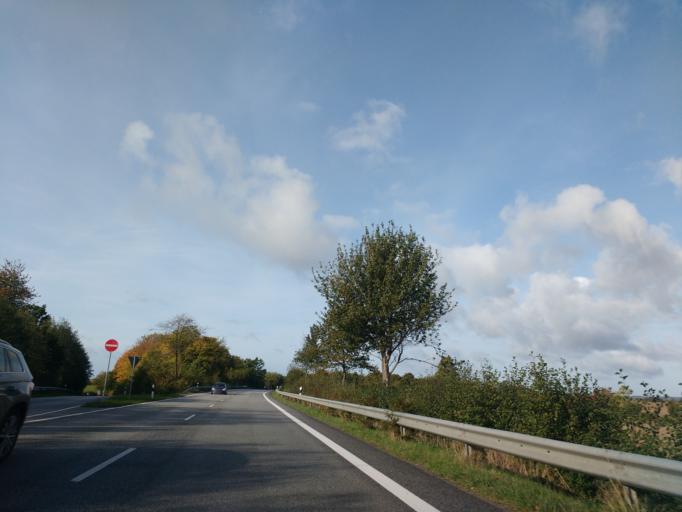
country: DE
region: Schleswig-Holstein
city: Altenkrempe
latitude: 54.1200
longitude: 10.8475
